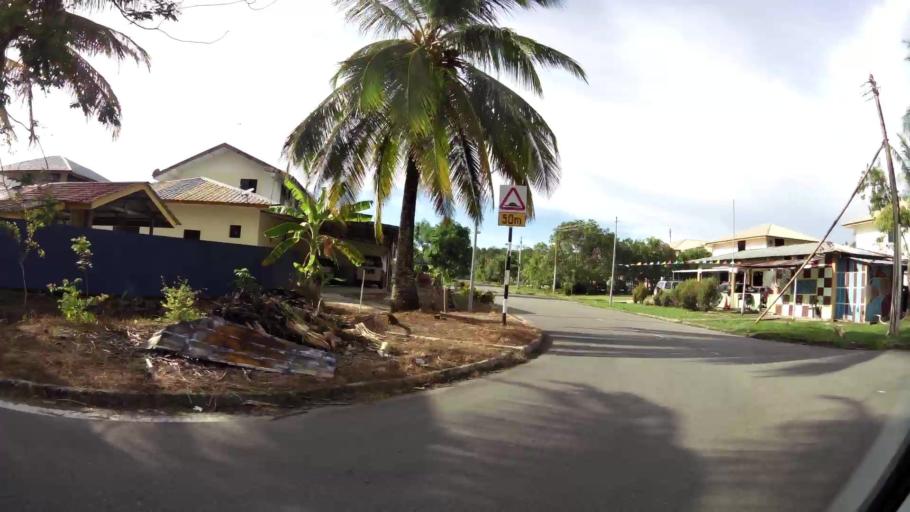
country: BN
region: Brunei and Muara
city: Bandar Seri Begawan
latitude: 4.9730
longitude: 115.0269
